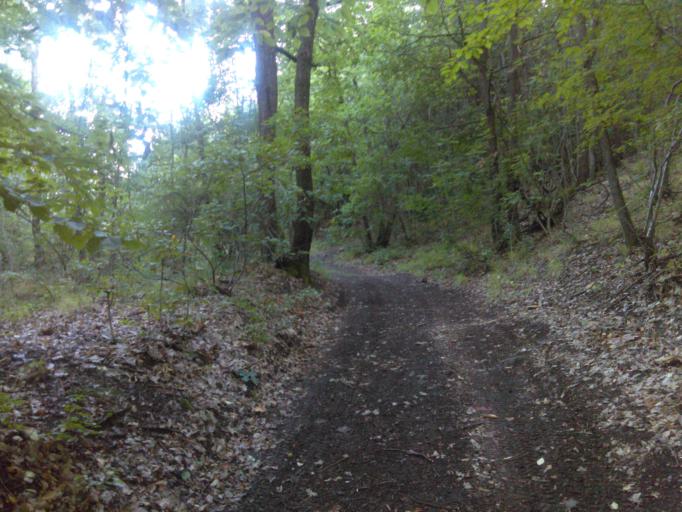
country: HU
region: Pest
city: Kismaros
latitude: 47.8352
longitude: 18.9902
